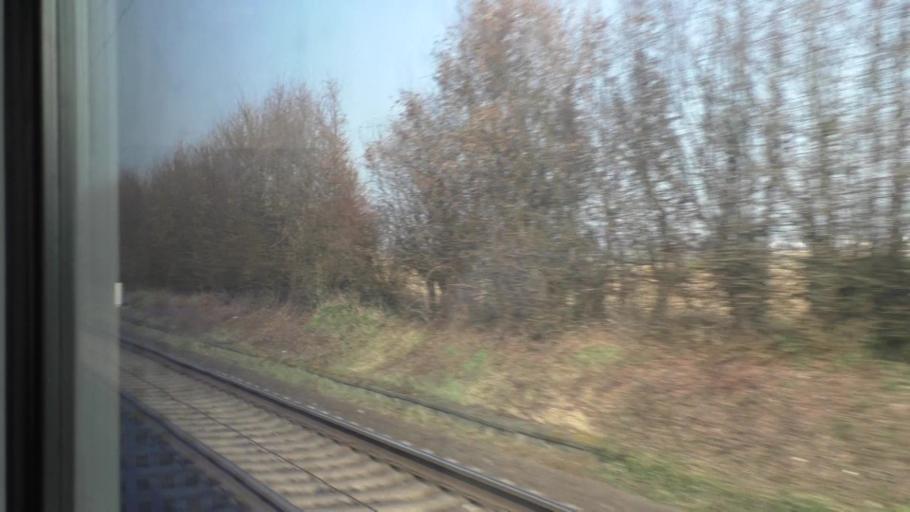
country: DE
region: Baden-Wuerttemberg
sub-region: Freiburg Region
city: Unterkrozingen
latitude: 47.9044
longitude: 7.6761
